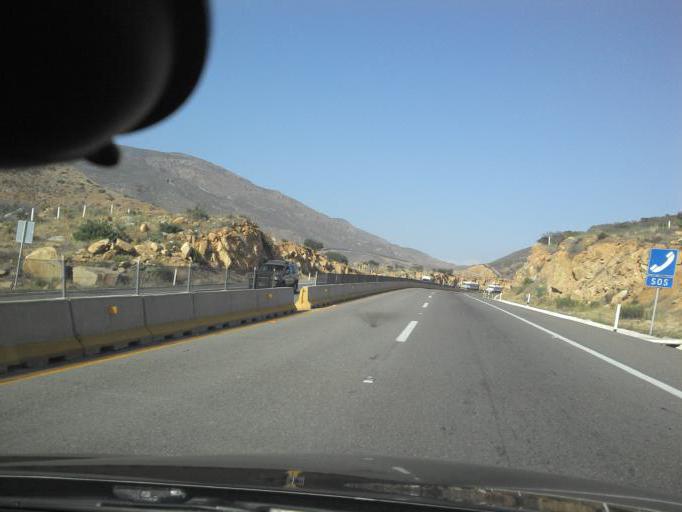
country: MX
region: Baja California
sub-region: Tijuana
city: Ejido Javier Rojo Gomez
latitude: 32.5520
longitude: -116.8403
